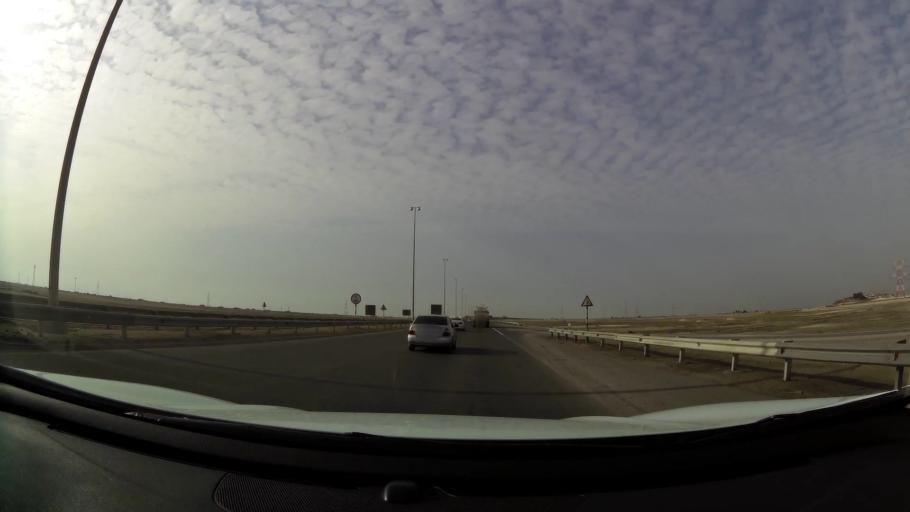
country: AE
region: Abu Dhabi
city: Abu Dhabi
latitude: 24.2043
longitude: 54.4196
